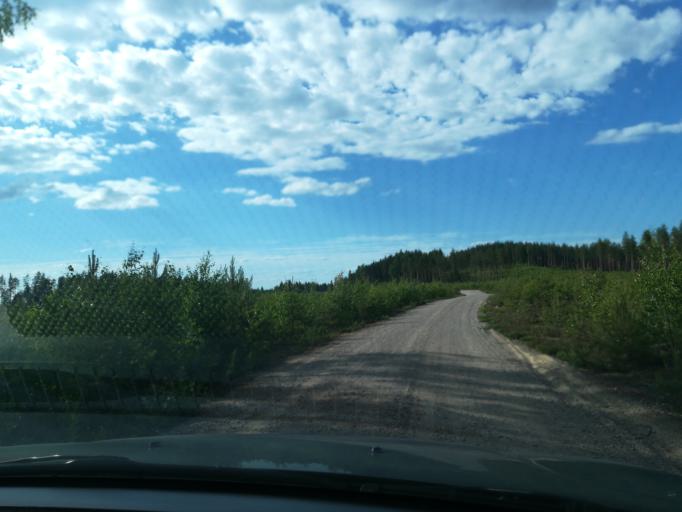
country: FI
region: Southern Savonia
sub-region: Savonlinna
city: Savonlinna
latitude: 61.6372
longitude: 28.7273
